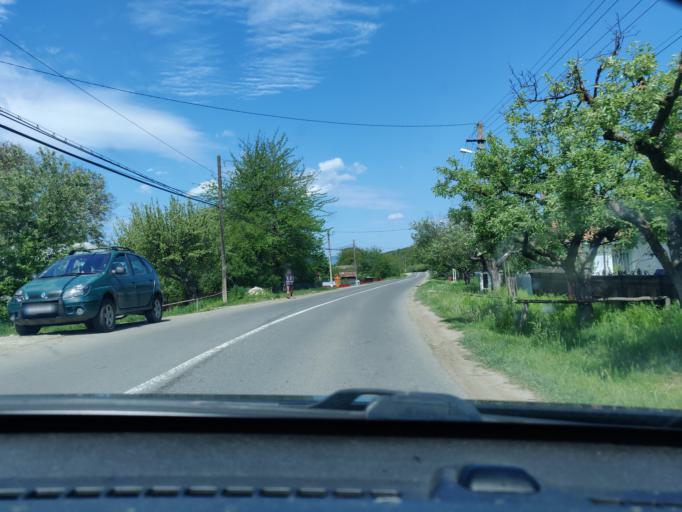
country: RO
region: Vrancea
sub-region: Comuna Campuri
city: Campuri
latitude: 46.0146
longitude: 26.7874
